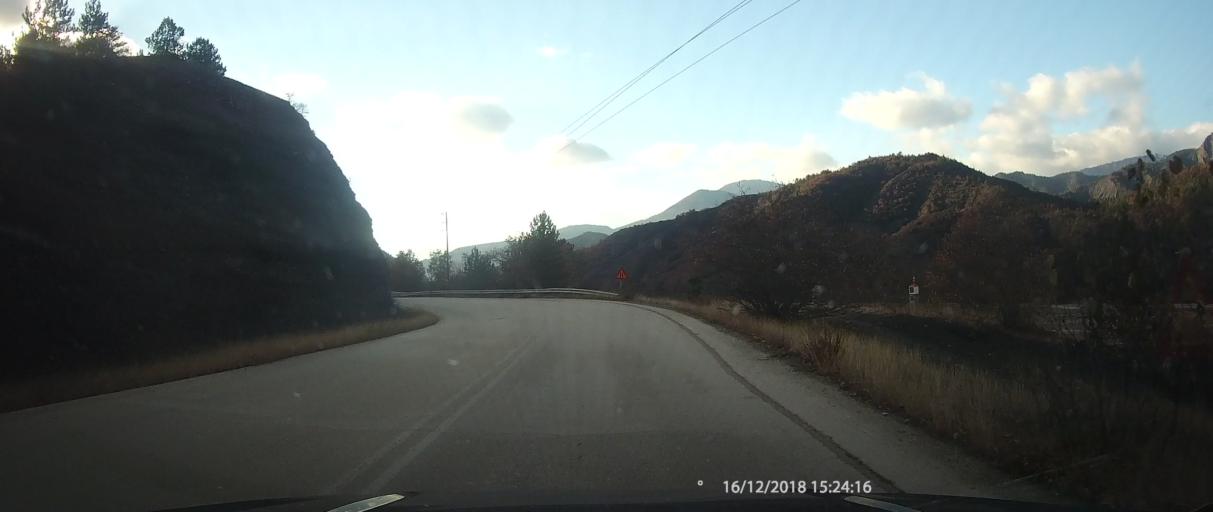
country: GR
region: Epirus
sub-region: Nomos Ioanninon
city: Konitsa
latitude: 40.1395
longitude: 20.7938
